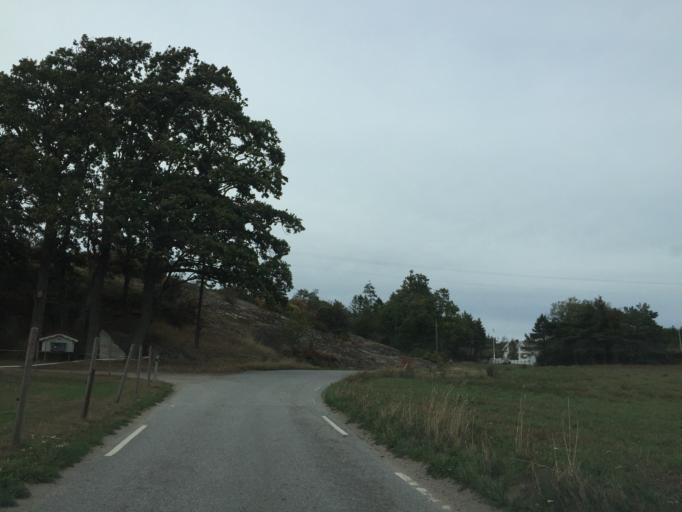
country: NO
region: Ostfold
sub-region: Hvaler
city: Skjaerhalden
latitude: 59.0481
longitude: 11.0439
